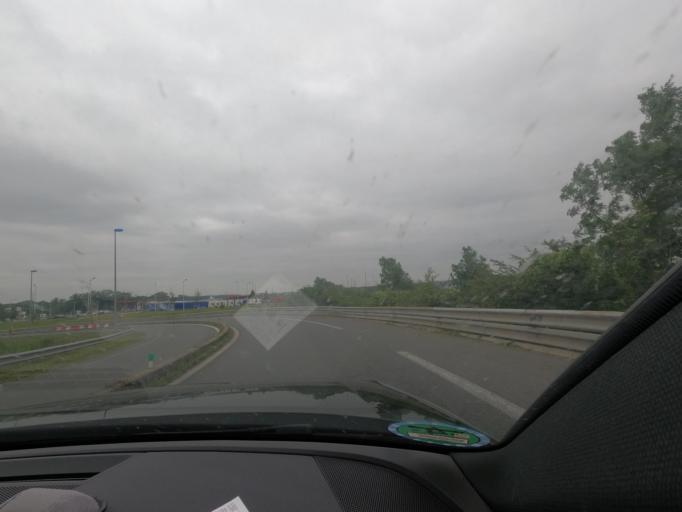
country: FR
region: Picardie
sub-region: Departement de l'Oise
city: Ressons-sur-Matz
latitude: 49.5217
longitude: 2.7234
